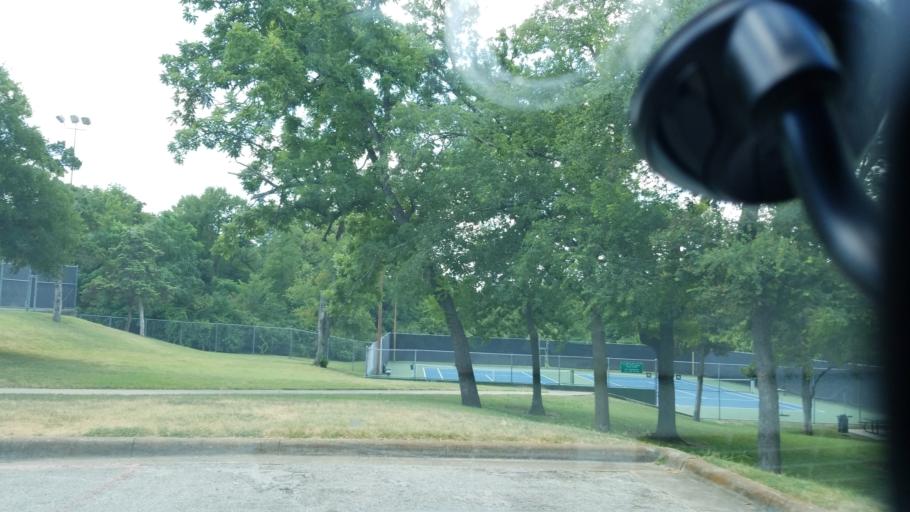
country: US
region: Texas
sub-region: Dallas County
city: Cockrell Hill
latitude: 32.7050
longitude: -96.8551
